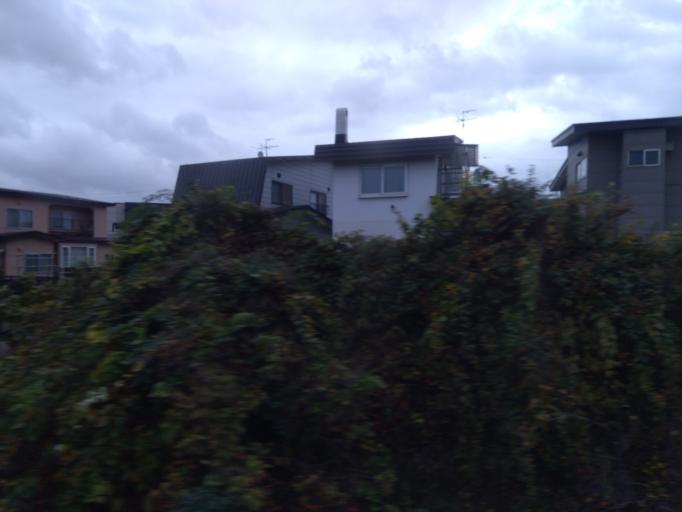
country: JP
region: Hokkaido
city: Hakodate
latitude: 41.8090
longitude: 140.7325
